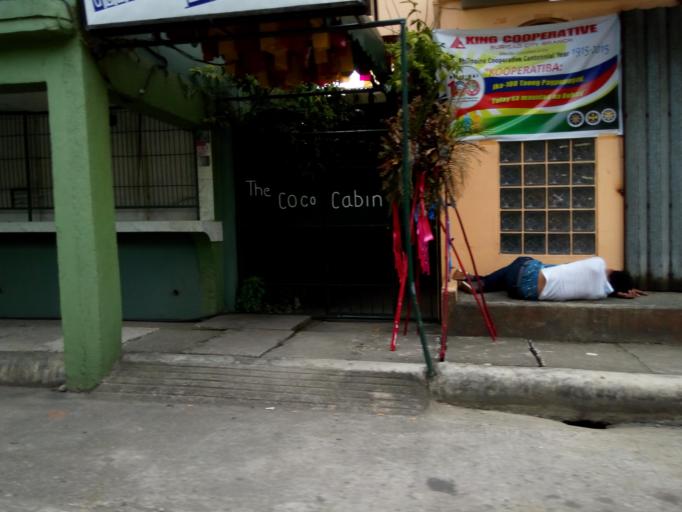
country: PH
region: Caraga
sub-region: Province of Surigao del Norte
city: Surigao
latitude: 9.7884
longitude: 125.4920
